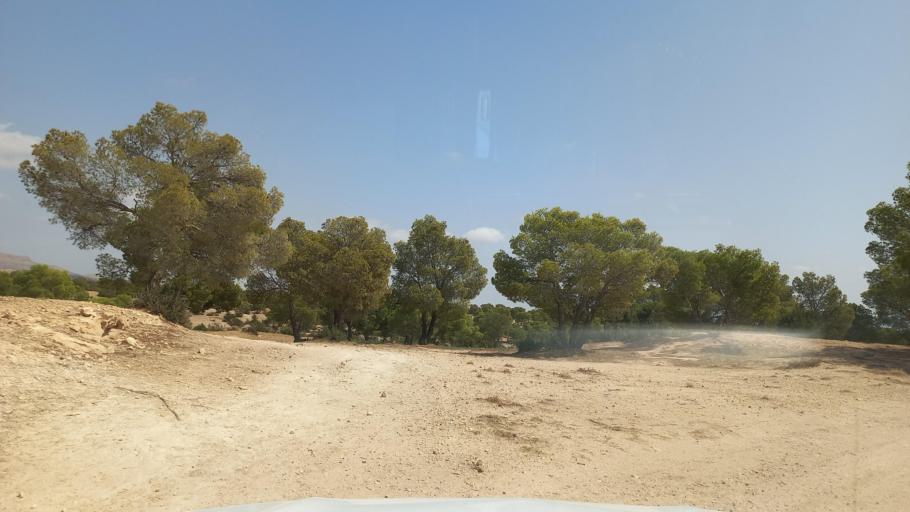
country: TN
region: Al Qasrayn
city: Sbiba
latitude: 35.3983
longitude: 8.9854
